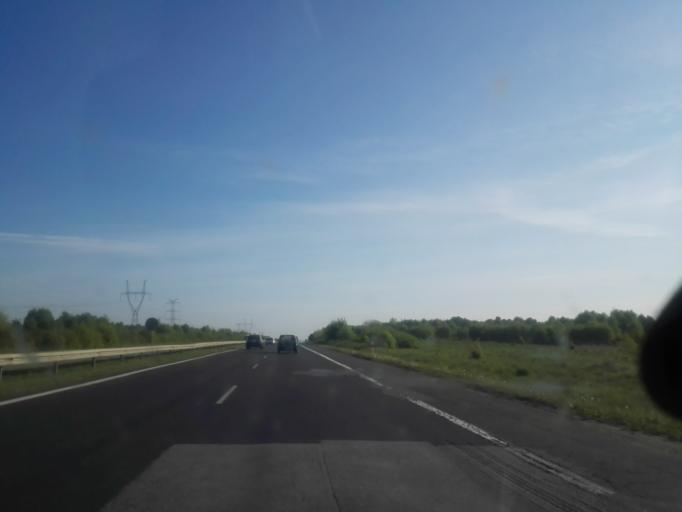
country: PL
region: Lodz Voivodeship
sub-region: Powiat radomszczanski
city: Radomsko
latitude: 51.0865
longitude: 19.3748
